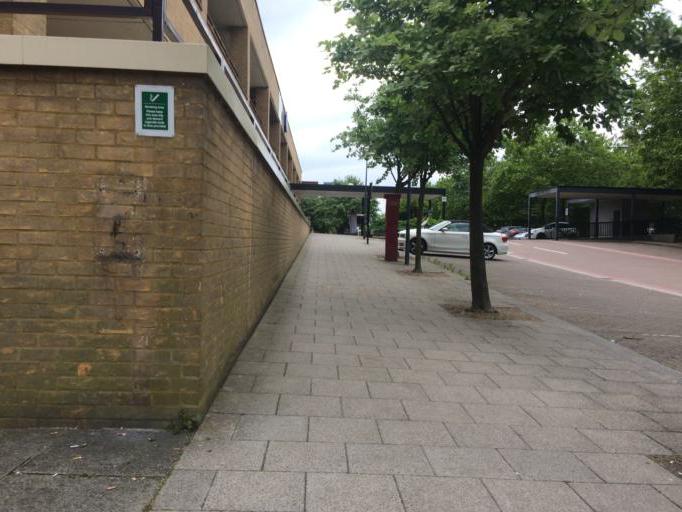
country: GB
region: England
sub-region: Milton Keynes
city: Milton Keynes
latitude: 52.0385
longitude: -0.7578
